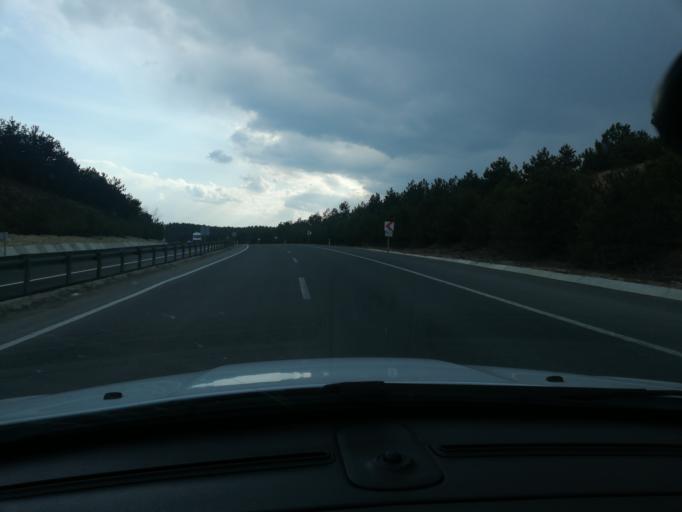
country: TR
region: Kastamonu
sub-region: Cide
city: Kastamonu
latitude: 41.4181
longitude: 33.7693
